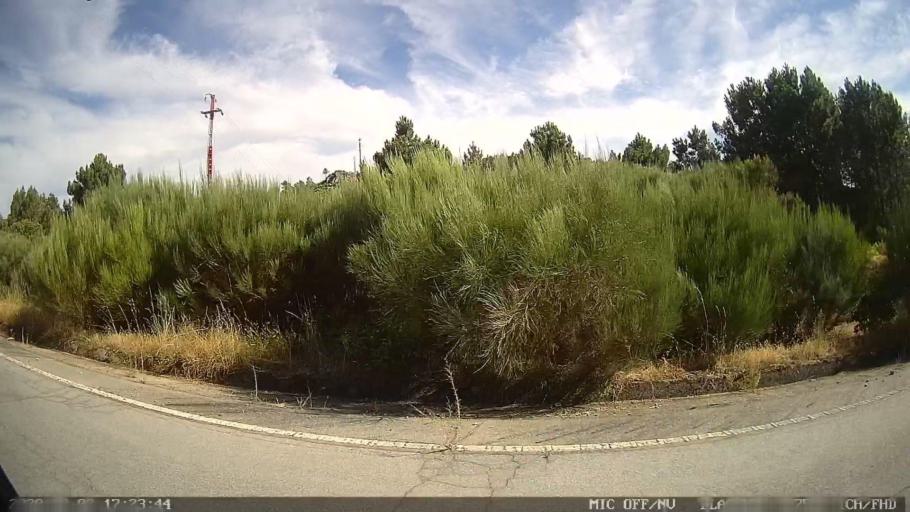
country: PT
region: Vila Real
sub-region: Sabrosa
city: Sabrosa
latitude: 41.3579
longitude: -7.5712
